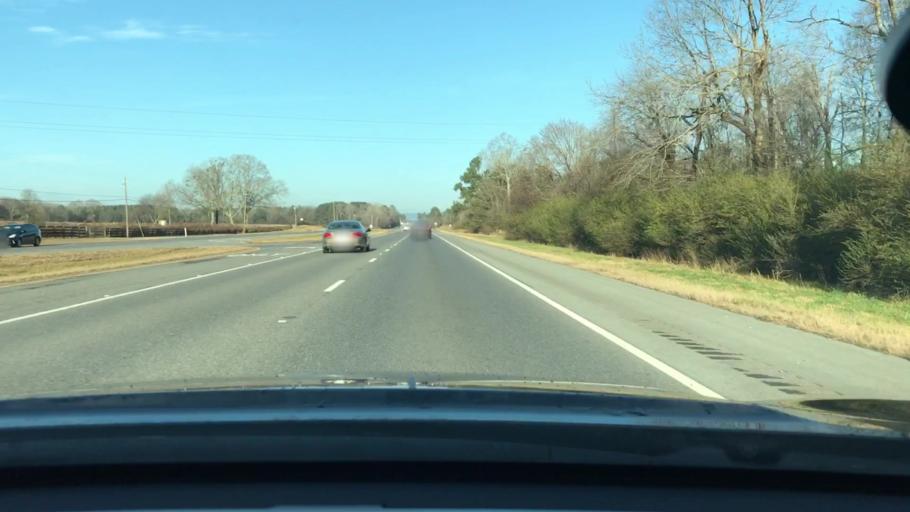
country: US
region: Alabama
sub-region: Shelby County
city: Harpersville
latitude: 33.3233
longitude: -86.4040
